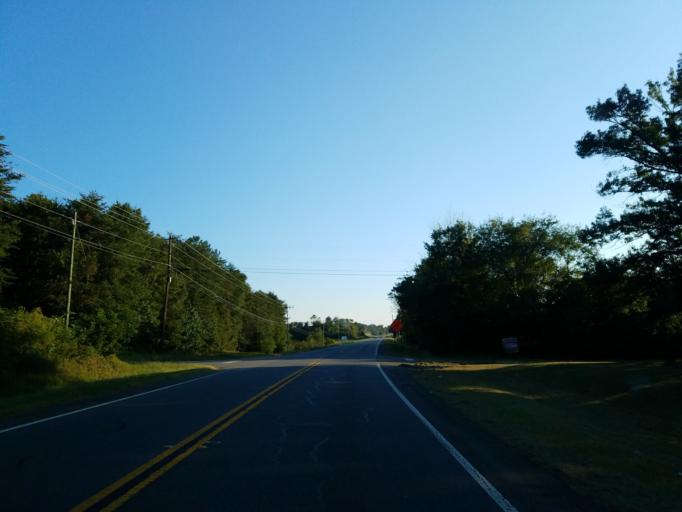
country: US
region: Georgia
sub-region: Bartow County
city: Rydal
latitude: 34.3341
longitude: -84.7155
